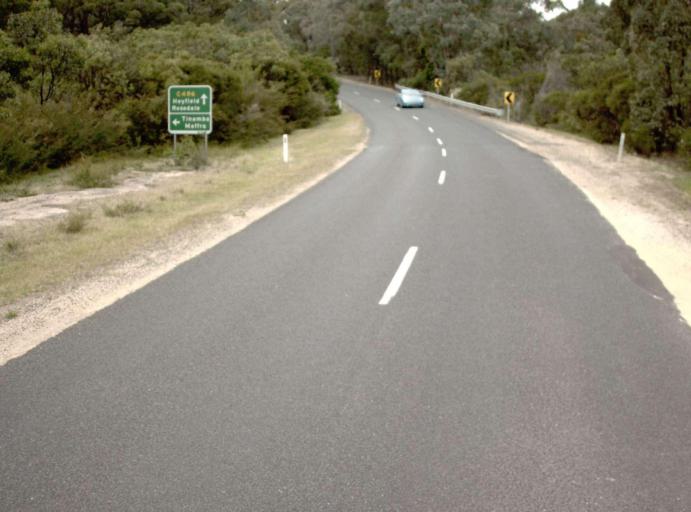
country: AU
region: Victoria
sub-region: Wellington
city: Heyfield
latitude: -37.9286
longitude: 146.7551
